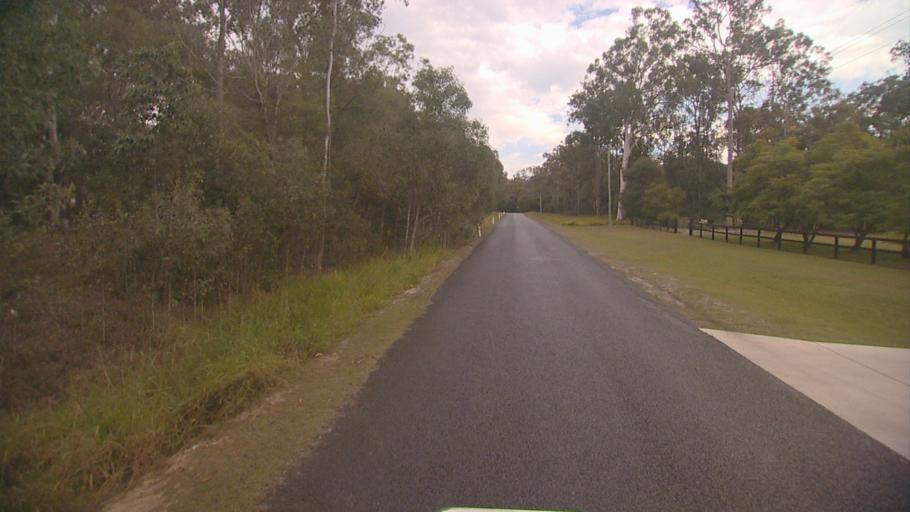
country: AU
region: Queensland
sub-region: Logan
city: Chambers Flat
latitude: -27.7848
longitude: 153.1094
